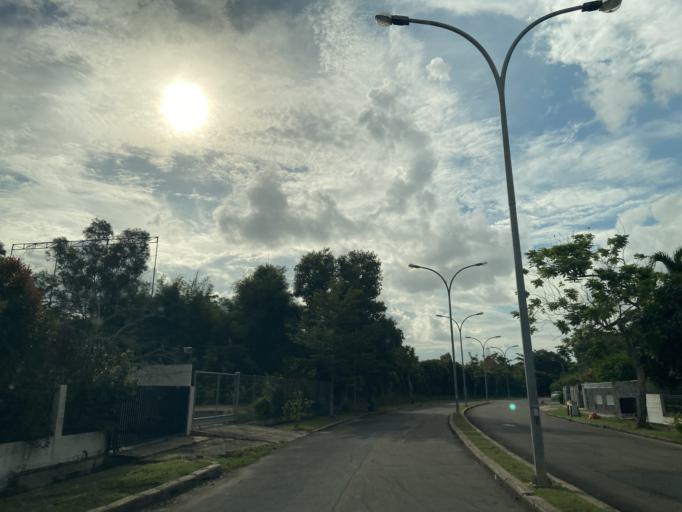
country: SG
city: Singapore
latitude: 1.1096
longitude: 104.0247
